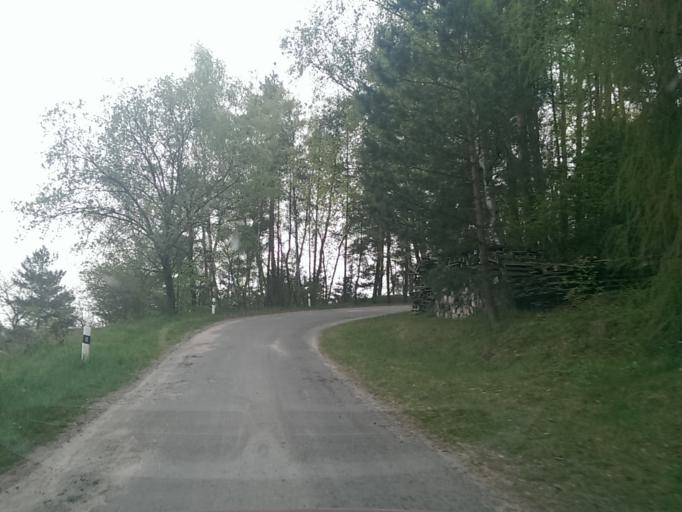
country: CZ
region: Liberecky
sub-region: Okres Semily
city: Turnov
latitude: 50.5500
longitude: 15.1238
